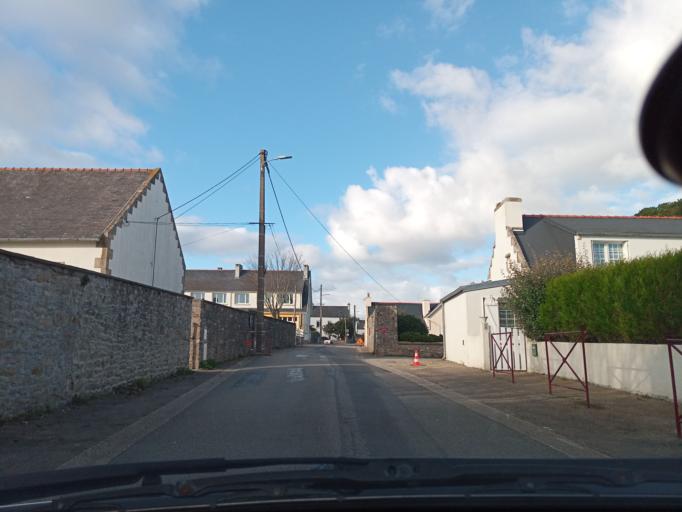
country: FR
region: Brittany
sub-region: Departement du Finistere
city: Plouhinec
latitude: 48.0146
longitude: -4.4913
